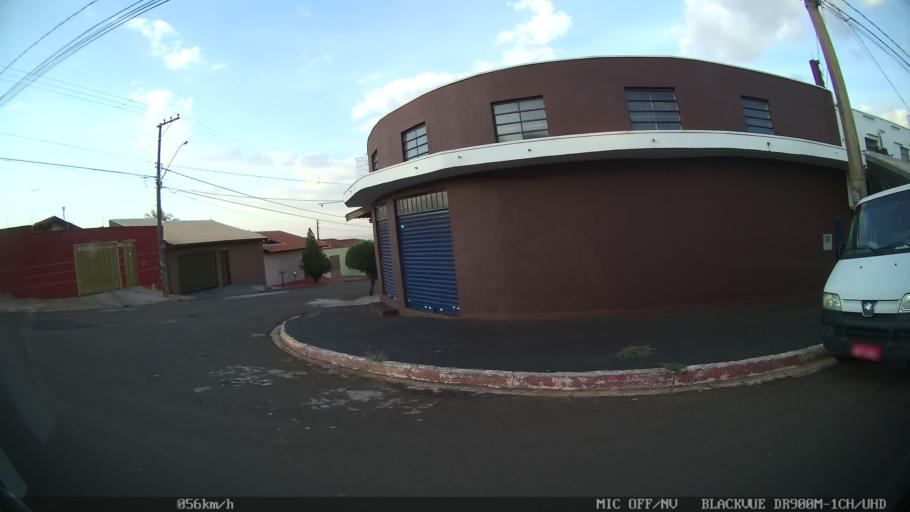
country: BR
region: Sao Paulo
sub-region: Ribeirao Preto
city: Ribeirao Preto
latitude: -21.1449
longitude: -47.8532
